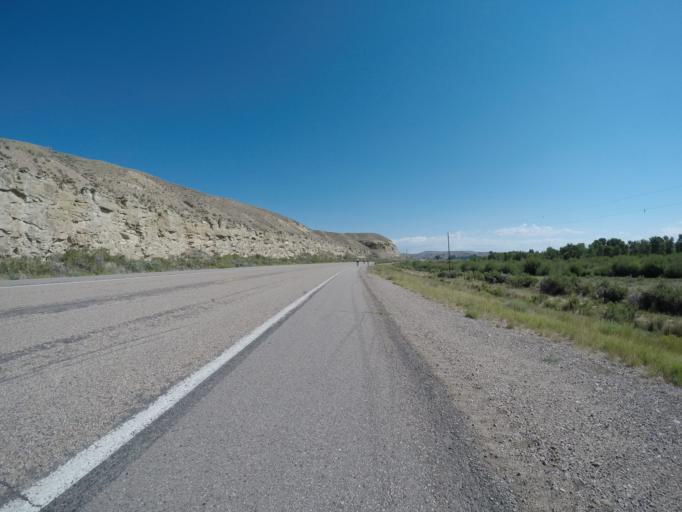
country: US
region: Wyoming
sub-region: Sublette County
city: Marbleton
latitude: 42.1784
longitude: -110.1864
